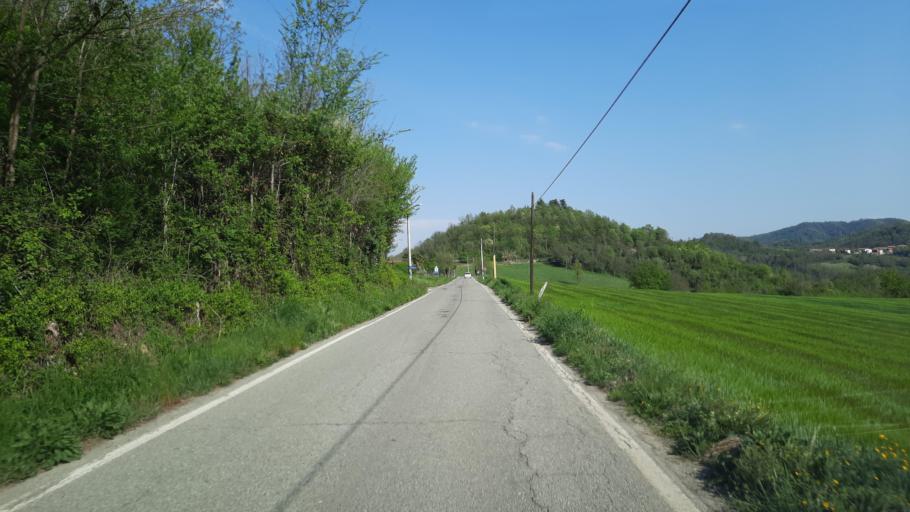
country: IT
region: Piedmont
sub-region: Provincia di Torino
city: Valentino
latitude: 45.1635
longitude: 8.0998
